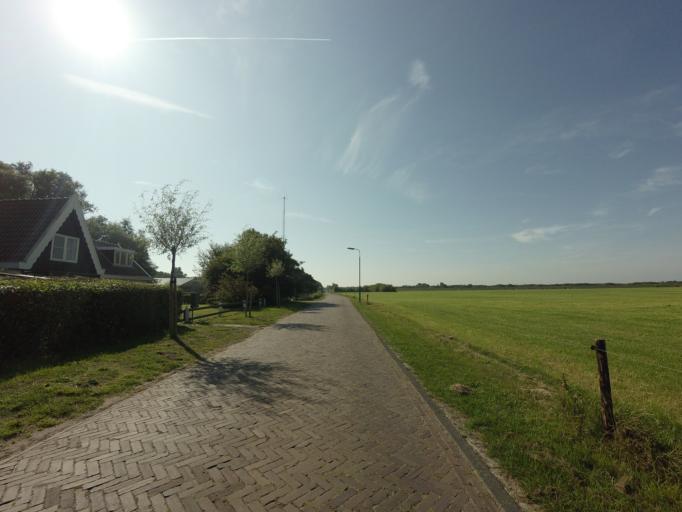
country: NL
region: Friesland
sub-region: Gemeente Schiermonnikoog
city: Schiermonnikoog
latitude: 53.4776
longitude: 6.1544
